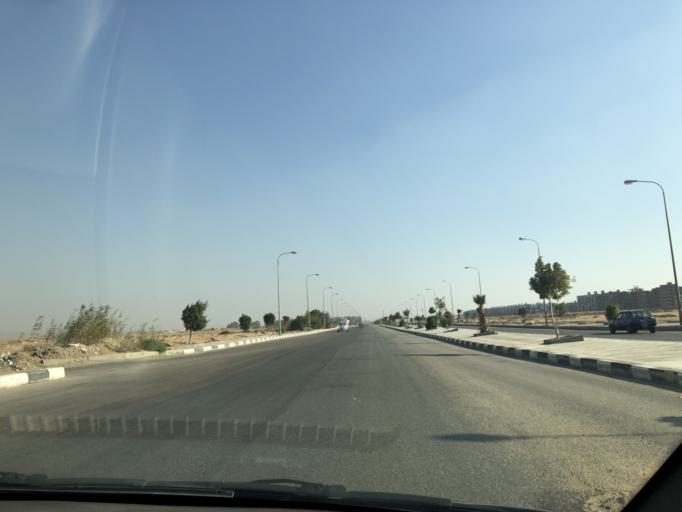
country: EG
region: Al Jizah
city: Madinat Sittah Uktubar
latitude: 29.9168
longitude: 31.0642
